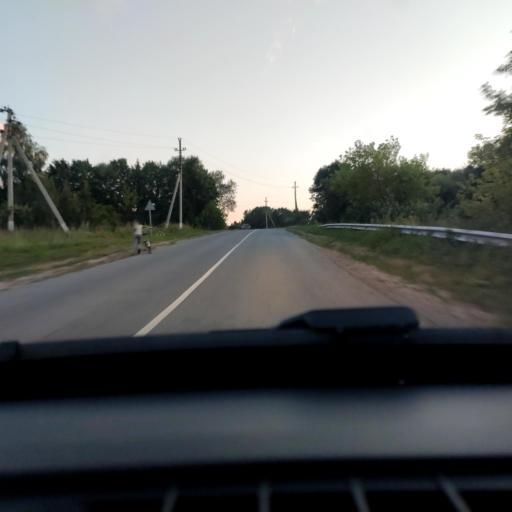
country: RU
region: Lipetsk
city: Zadonsk
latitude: 52.2917
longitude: 38.7615
